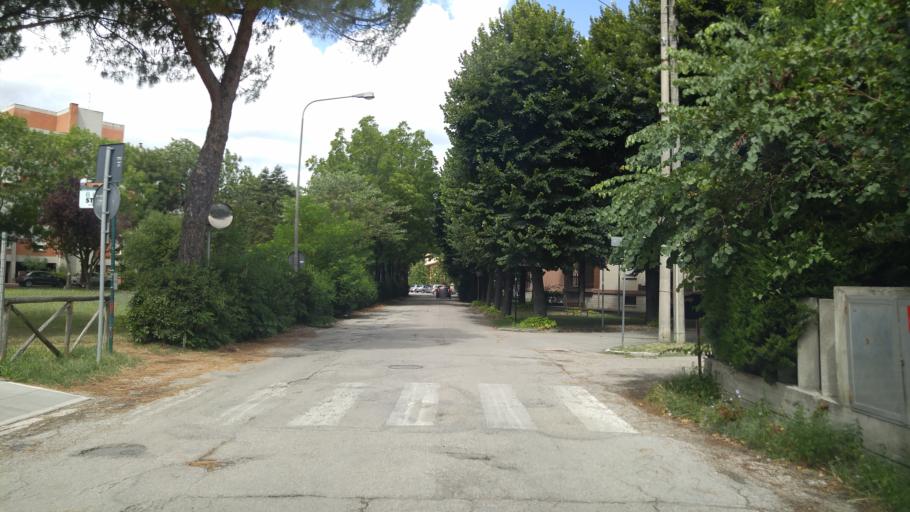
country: IT
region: The Marches
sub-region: Provincia di Pesaro e Urbino
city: Fano
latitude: 43.8390
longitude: 13.0055
